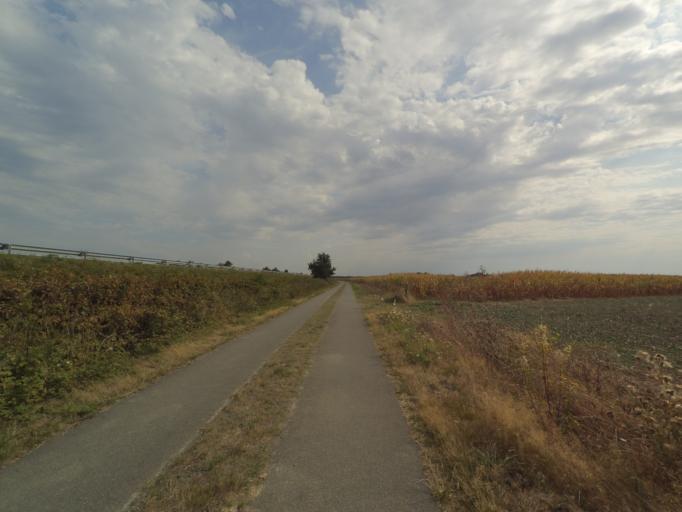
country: FR
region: Pays de la Loire
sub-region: Departement de la Vendee
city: Bouffere
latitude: 46.9885
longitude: -1.3811
